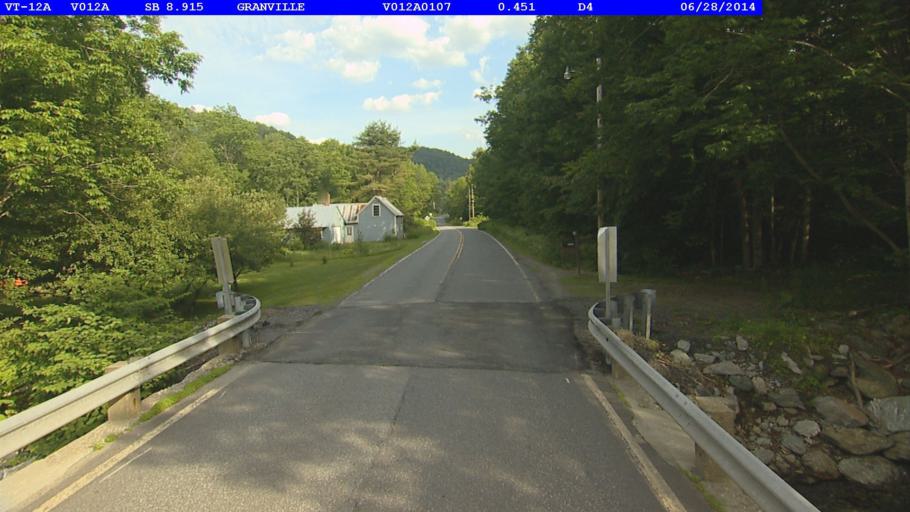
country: US
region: Vermont
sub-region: Orange County
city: Randolph
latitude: 44.0166
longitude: -72.7588
